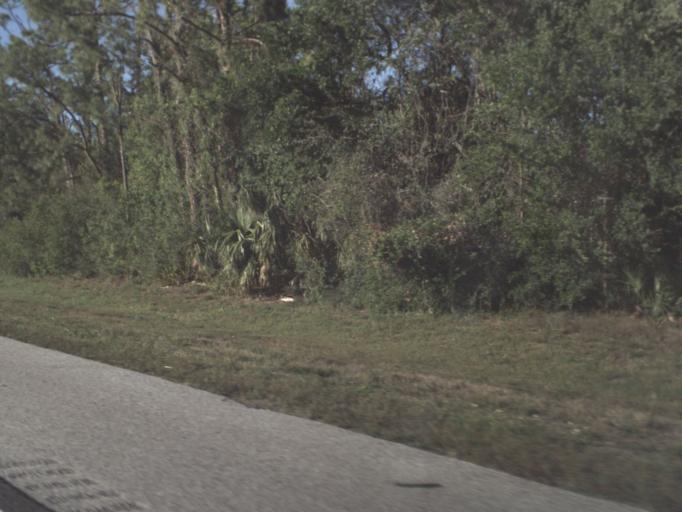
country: US
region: Florida
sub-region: Flagler County
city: Flagler Beach
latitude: 29.4072
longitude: -81.1565
